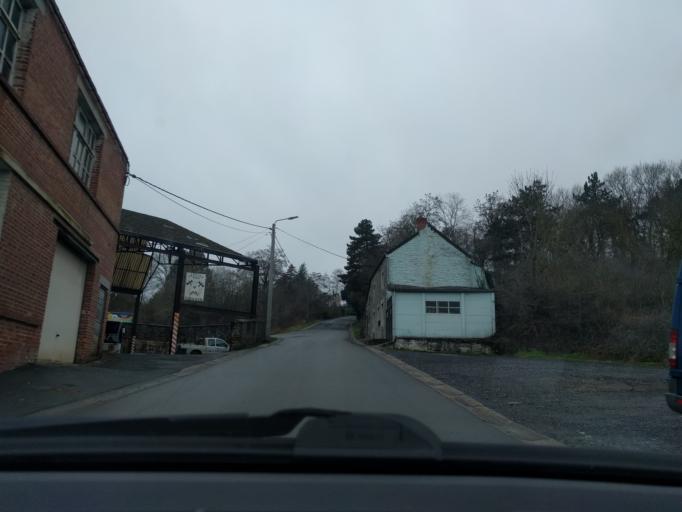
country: BE
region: Wallonia
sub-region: Province de Namur
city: Couvin
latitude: 50.0561
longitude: 4.4901
